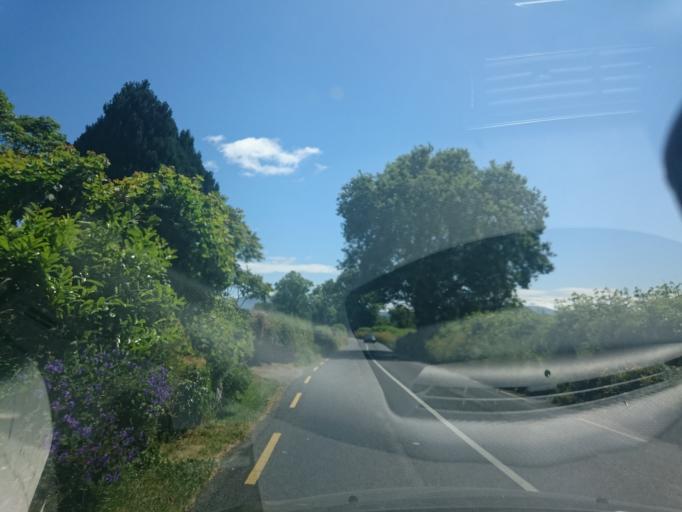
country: IE
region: Leinster
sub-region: County Carlow
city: Bagenalstown
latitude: 52.6285
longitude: -7.0317
